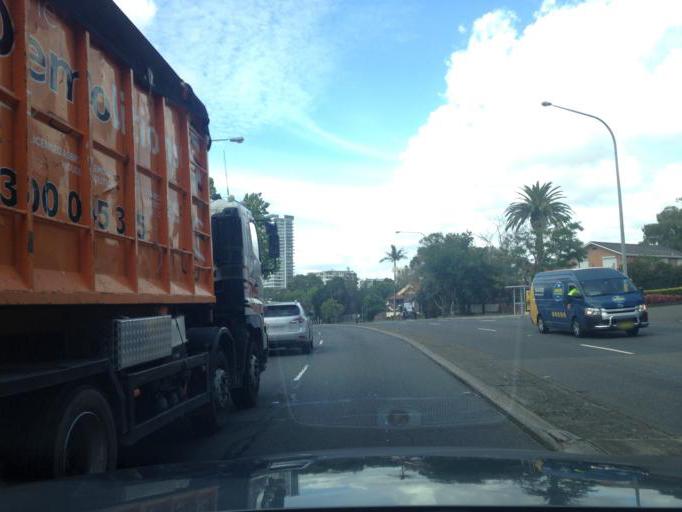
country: AU
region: New South Wales
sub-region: Canada Bay
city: Rhodes
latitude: -33.8273
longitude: 151.0902
